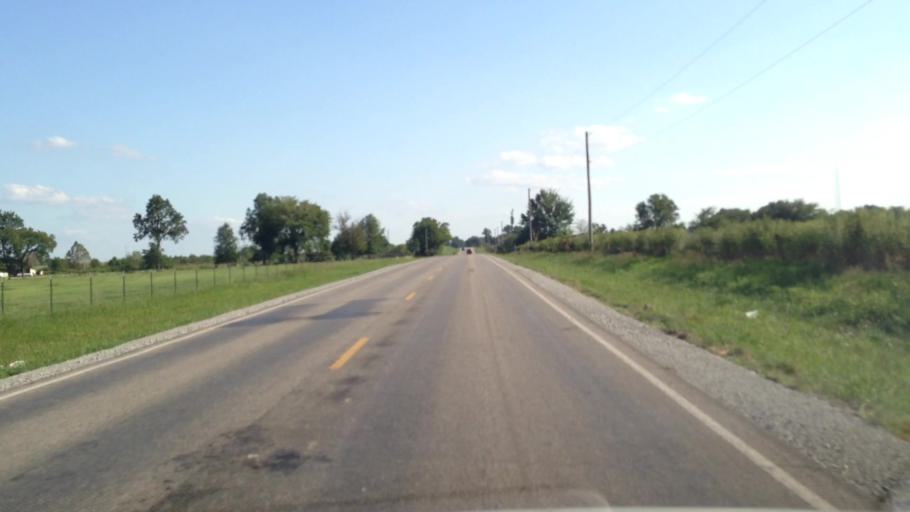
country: US
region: Kansas
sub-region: Crawford County
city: Pittsburg
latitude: 37.3477
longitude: -94.6316
